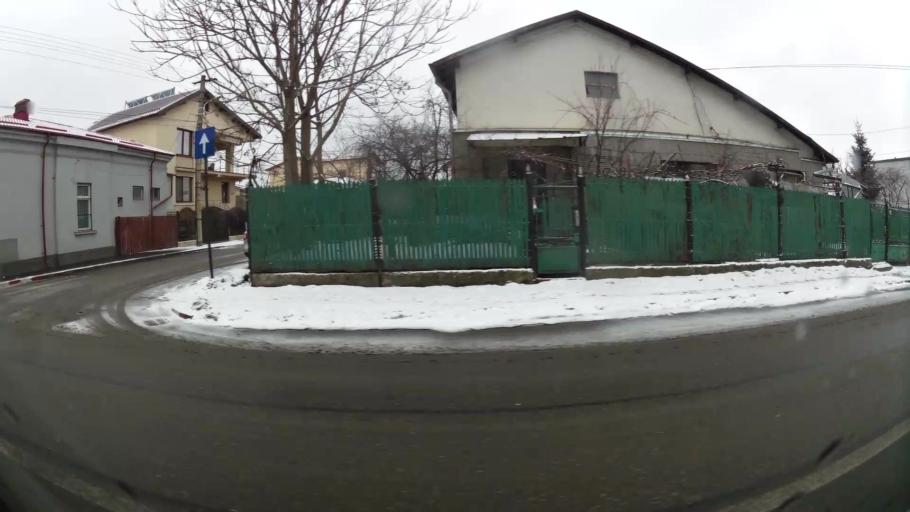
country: RO
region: Prahova
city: Ploiesti
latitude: 44.9350
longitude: 26.0168
